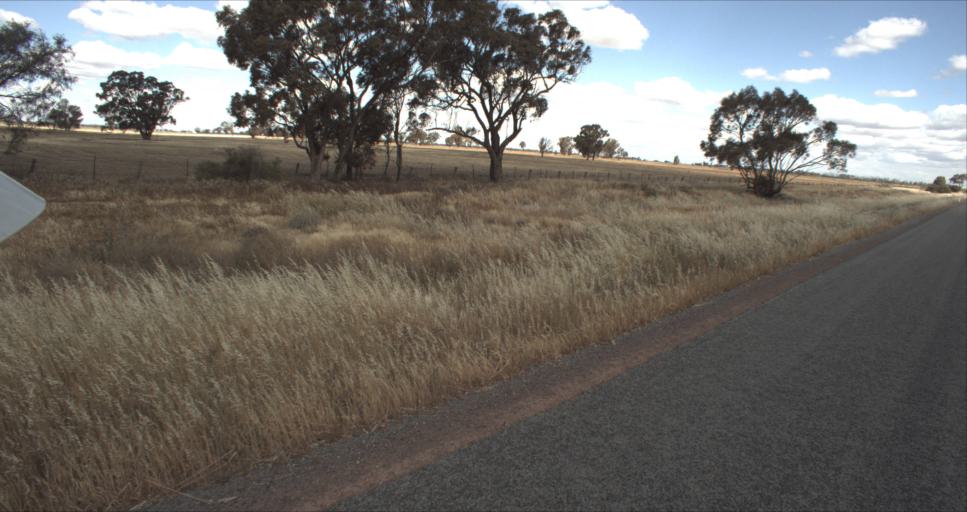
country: AU
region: New South Wales
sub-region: Leeton
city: Leeton
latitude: -34.4880
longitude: 146.2478
